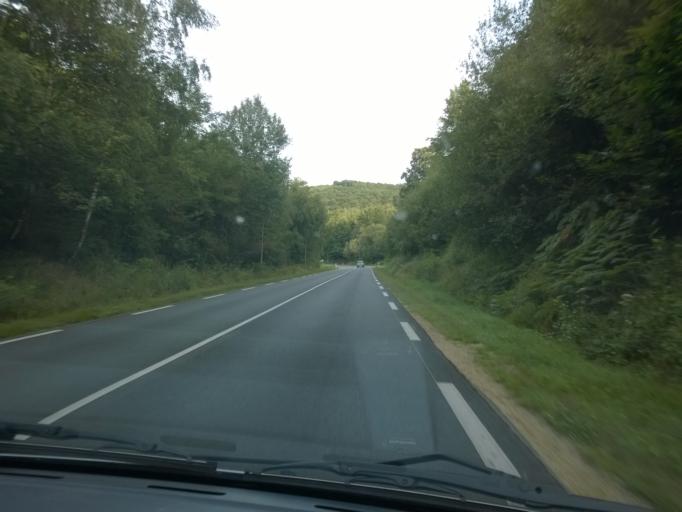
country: FR
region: Limousin
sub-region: Departement de la Haute-Vienne
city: Saint-Leonard-de-Noblat
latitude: 45.7795
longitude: 1.4989
